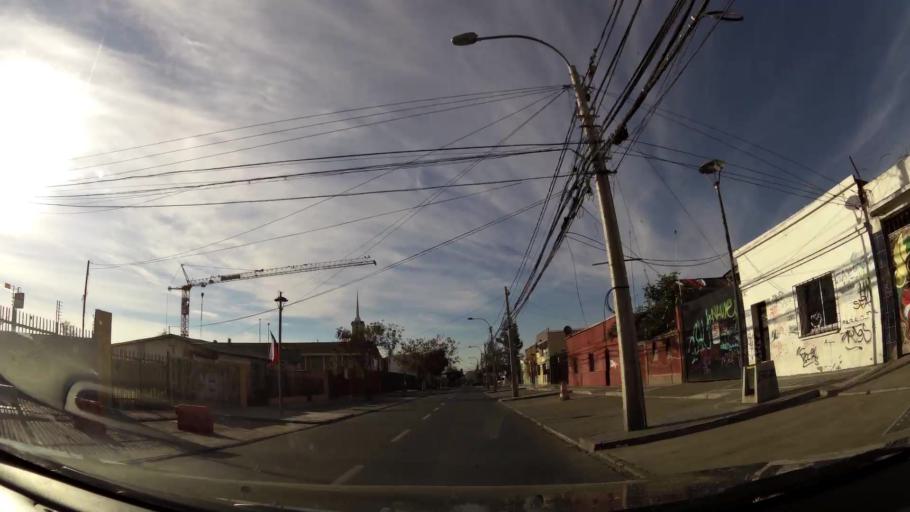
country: CL
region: Santiago Metropolitan
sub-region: Provincia de Cordillera
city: Puente Alto
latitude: -33.6068
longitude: -70.5736
